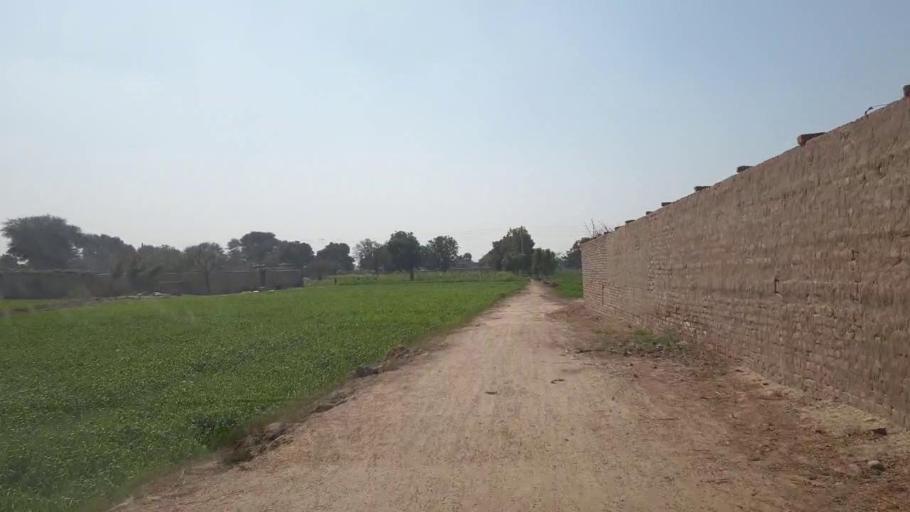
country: PK
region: Sindh
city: Tando Jam
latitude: 25.3276
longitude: 68.6320
